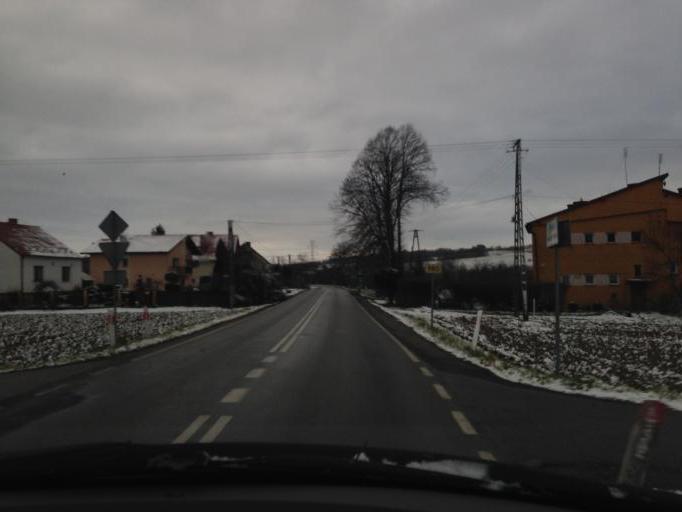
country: PL
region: Lesser Poland Voivodeship
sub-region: Powiat tarnowski
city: Gromnik
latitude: 49.8419
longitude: 20.9758
